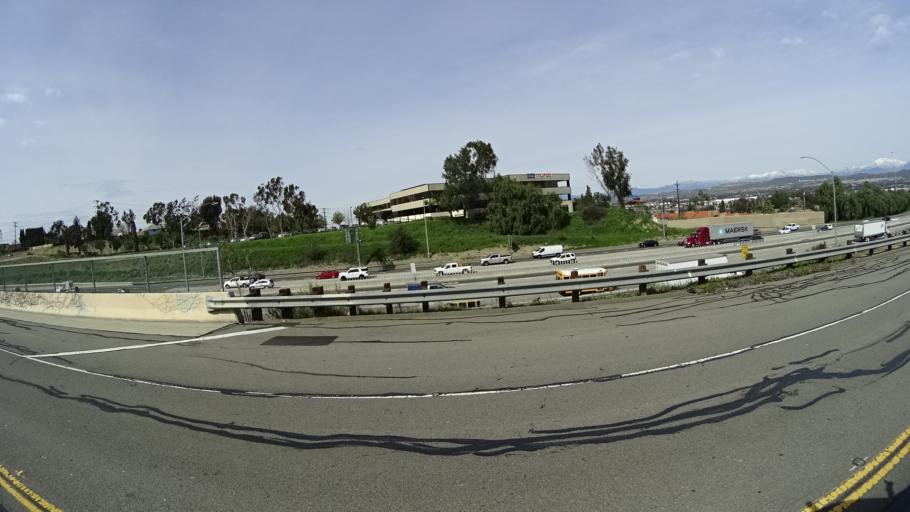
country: US
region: California
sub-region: Orange County
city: Villa Park
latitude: 33.8408
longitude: -117.8312
